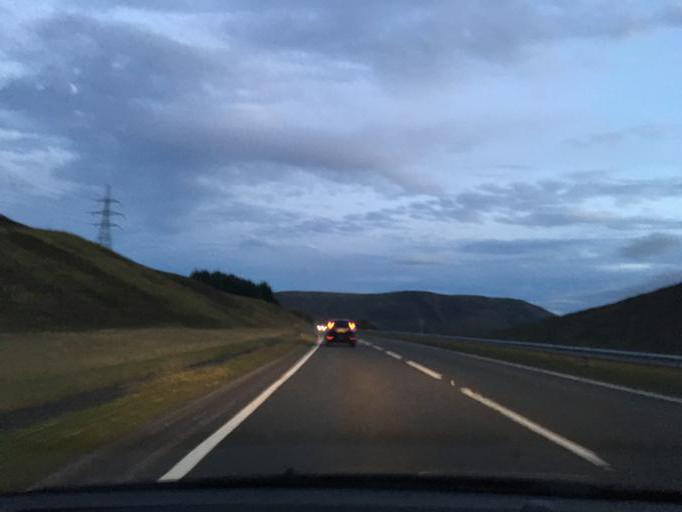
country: GB
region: Scotland
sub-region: Highland
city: Kingussie
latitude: 56.8500
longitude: -4.2433
